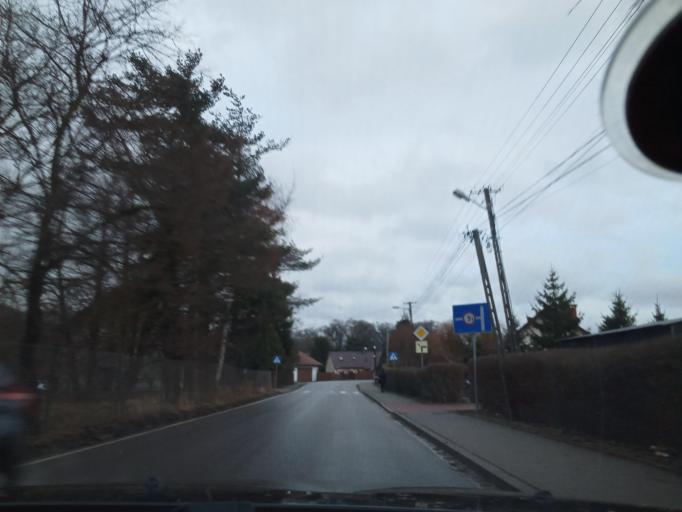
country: PL
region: Lesser Poland Voivodeship
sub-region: Powiat wielicki
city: Kokotow
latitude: 50.0071
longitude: 20.0859
